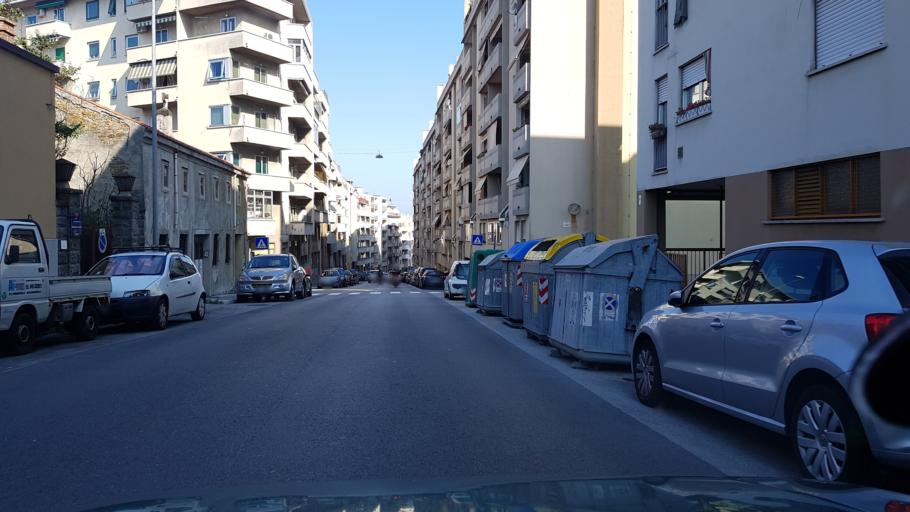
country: IT
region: Friuli Venezia Giulia
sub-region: Provincia di Trieste
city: Trieste
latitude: 45.6381
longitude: 13.7867
